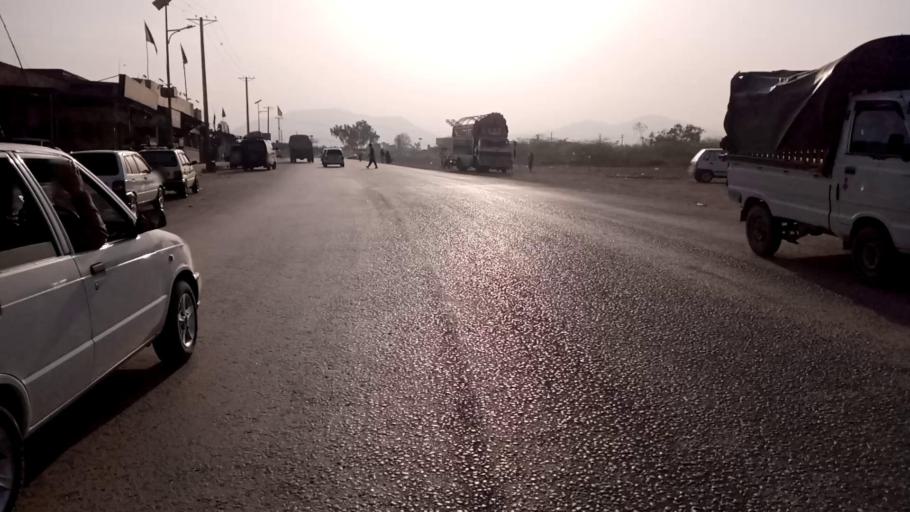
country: PK
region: Khyber Pakhtunkhwa
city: Peshawar
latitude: 33.9991
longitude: 71.4065
